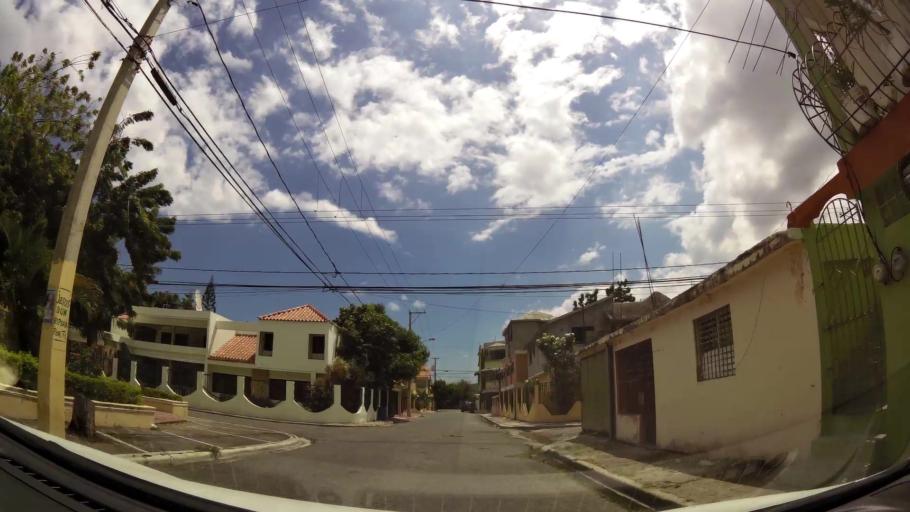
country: DO
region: San Cristobal
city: San Cristobal
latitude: 18.4136
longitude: -70.0991
